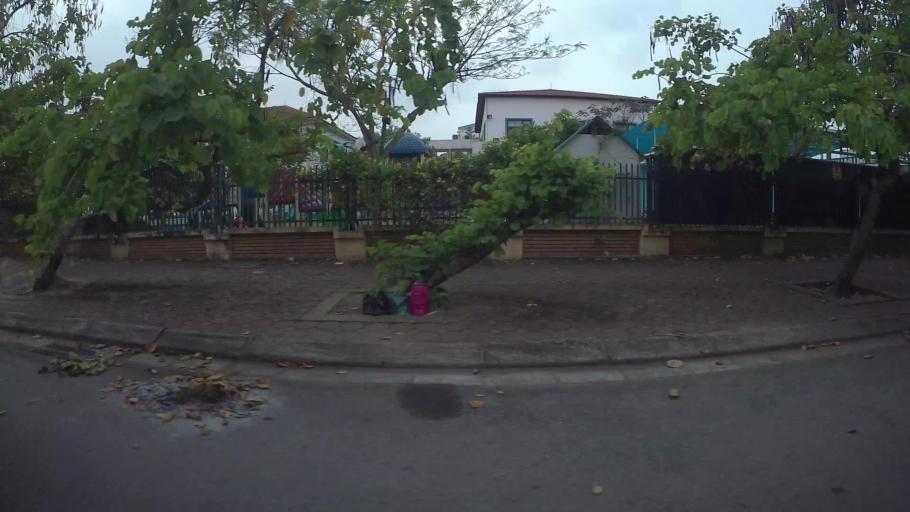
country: VN
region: Ha Noi
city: Trau Quy
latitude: 21.0625
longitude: 105.9105
